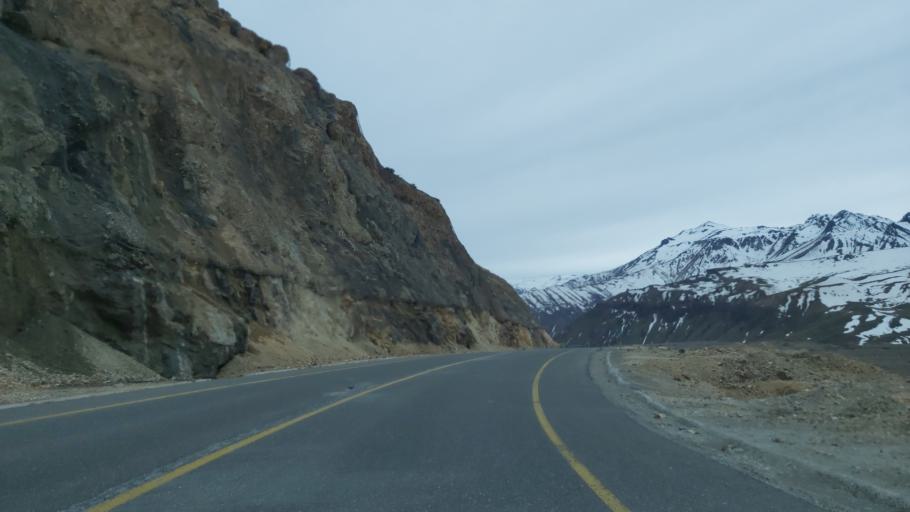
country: CL
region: Maule
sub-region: Provincia de Linares
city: Colbun
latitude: -35.9747
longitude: -70.5637
